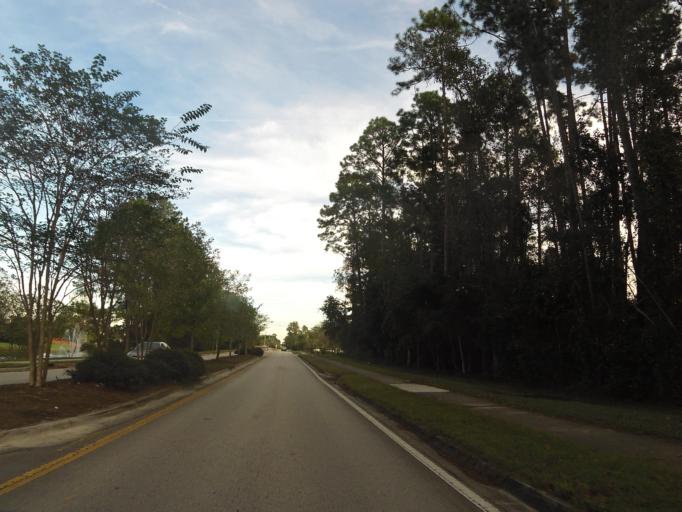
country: US
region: Florida
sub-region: Saint Johns County
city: Fruit Cove
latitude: 30.1615
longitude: -81.5695
